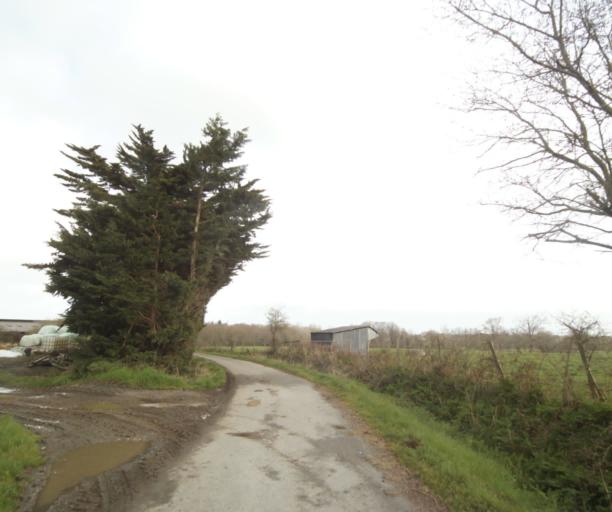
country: FR
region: Pays de la Loire
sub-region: Departement de la Loire-Atlantique
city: Bouvron
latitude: 47.4055
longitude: -1.8664
